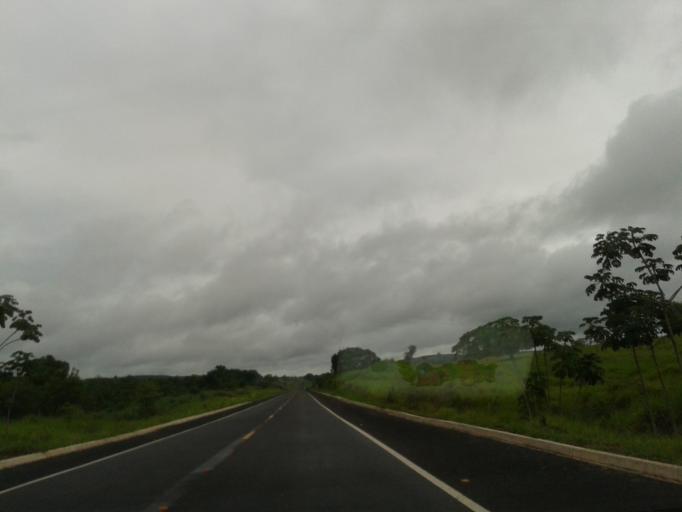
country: BR
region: Minas Gerais
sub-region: Santa Vitoria
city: Santa Vitoria
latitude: -19.2501
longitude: -50.0119
